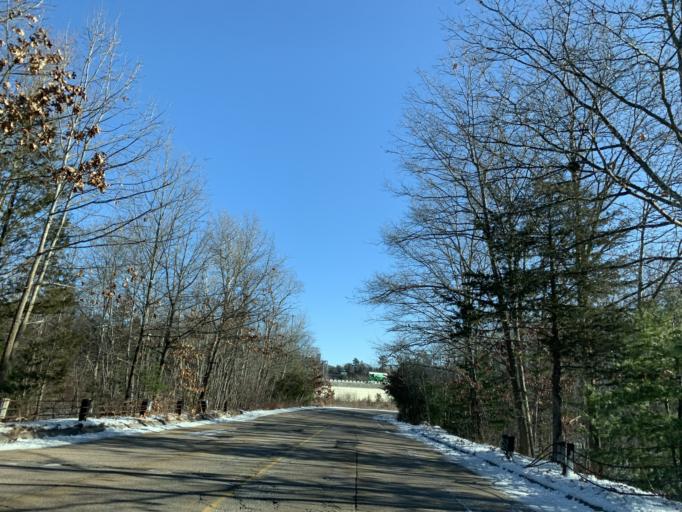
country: US
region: Massachusetts
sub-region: Norfolk County
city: Canton
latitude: 42.2045
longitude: -71.1380
